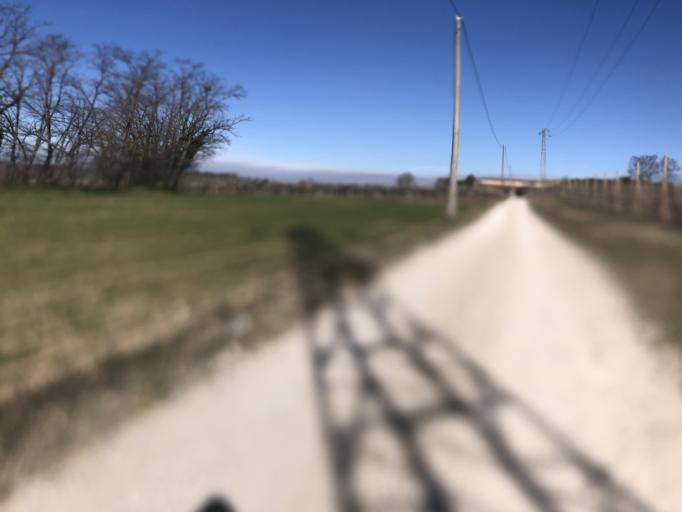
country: IT
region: Veneto
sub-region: Provincia di Verona
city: San Giorgio in Salici
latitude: 45.4252
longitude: 10.8085
